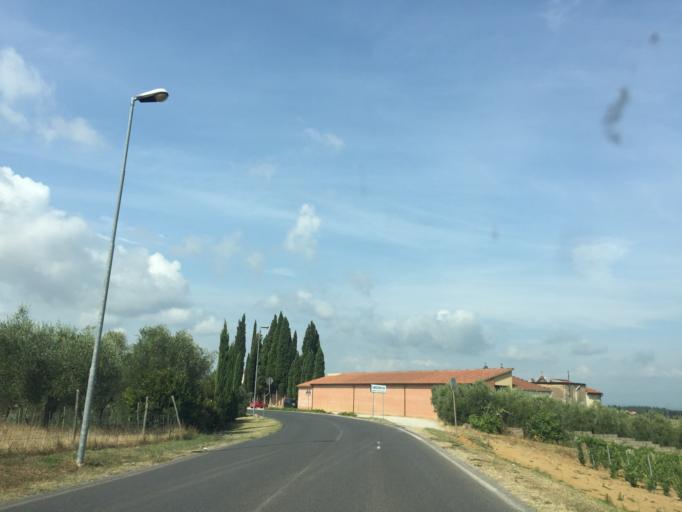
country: IT
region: Tuscany
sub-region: Province of Florence
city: Lazzeretto
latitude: 43.7869
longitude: 10.8675
